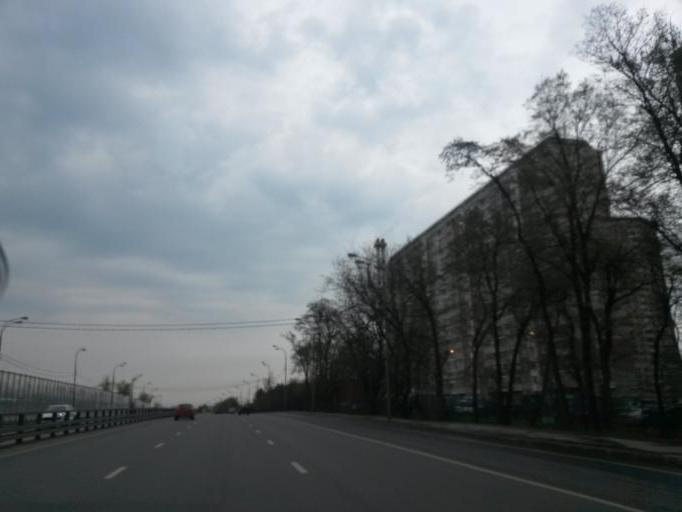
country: RU
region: Moscow
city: Annino
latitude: 55.5474
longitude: 37.5860
